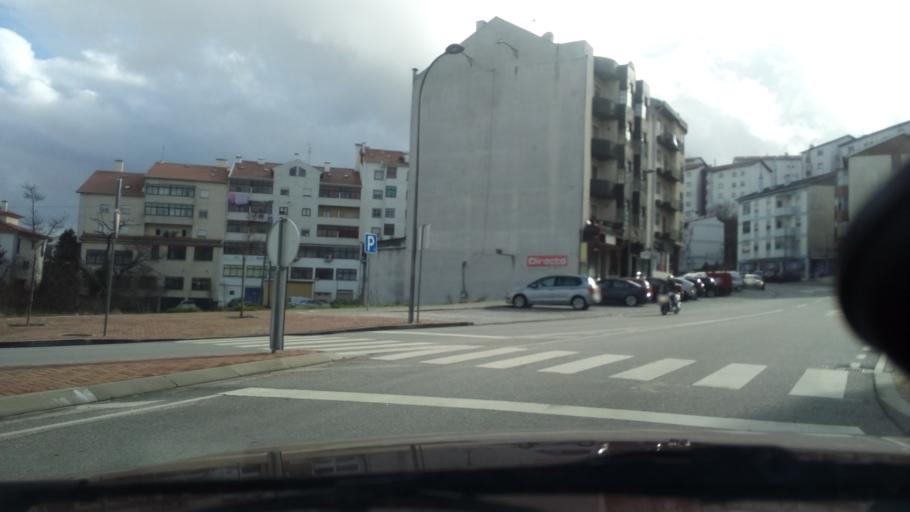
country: PT
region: Guarda
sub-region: Guarda
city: Guarda
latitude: 40.5393
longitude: -7.2618
